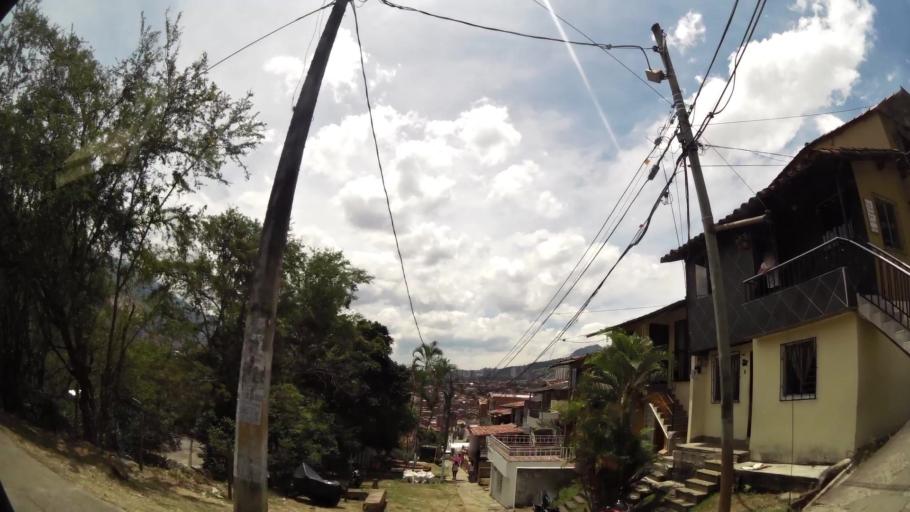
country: CO
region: Antioquia
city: Bello
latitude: 6.3462
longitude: -75.5587
